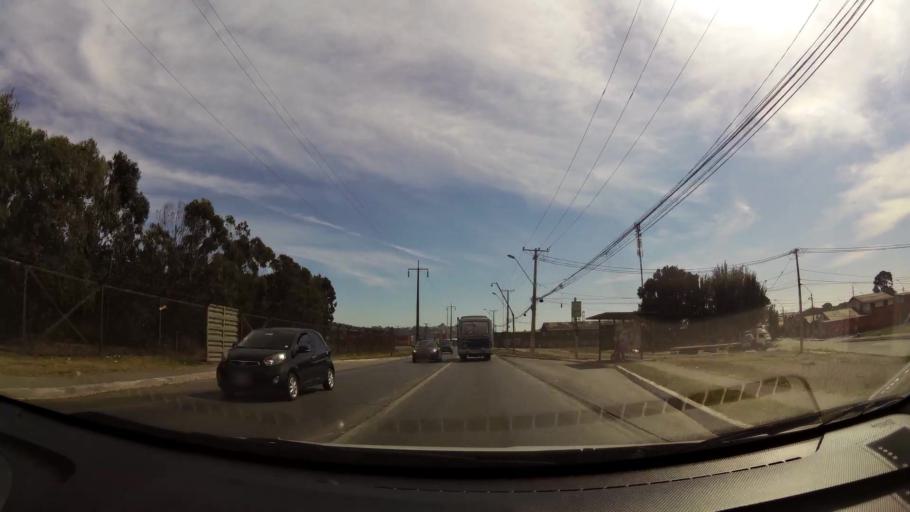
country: CL
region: Biobio
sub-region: Provincia de Concepcion
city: Talcahuano
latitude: -36.7307
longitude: -73.1181
